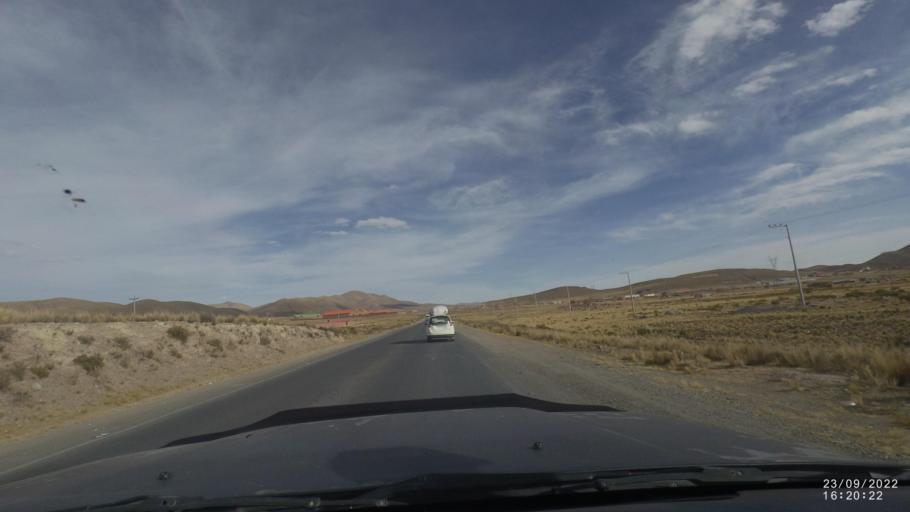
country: BO
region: Oruro
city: Machacamarca
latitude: -18.0355
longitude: -67.0182
